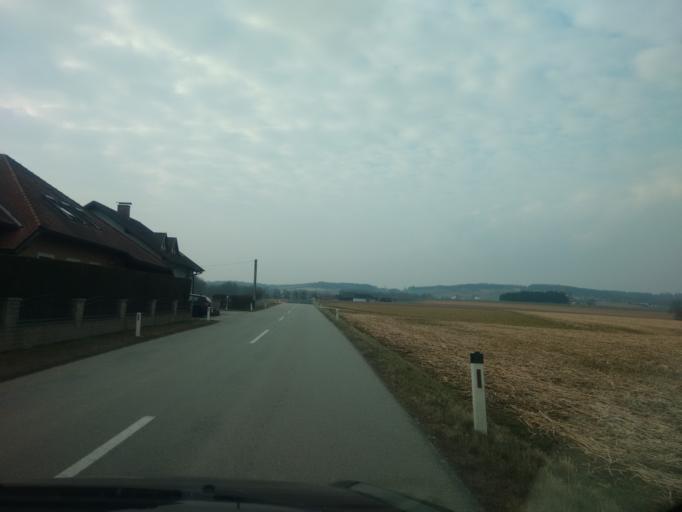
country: AT
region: Upper Austria
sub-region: Wels-Land
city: Holzhausen
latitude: 48.2210
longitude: 14.0767
